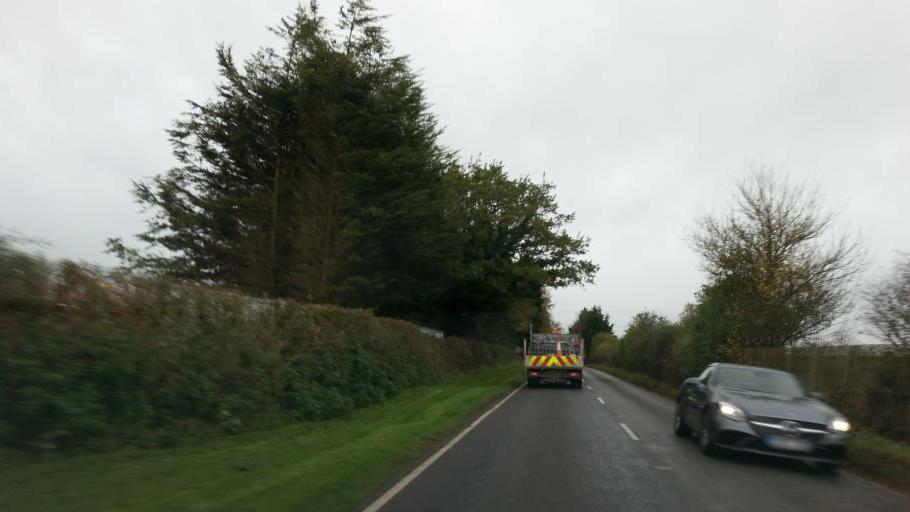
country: GB
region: England
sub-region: Northamptonshire
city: Rothwell
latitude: 52.4106
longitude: -0.8309
